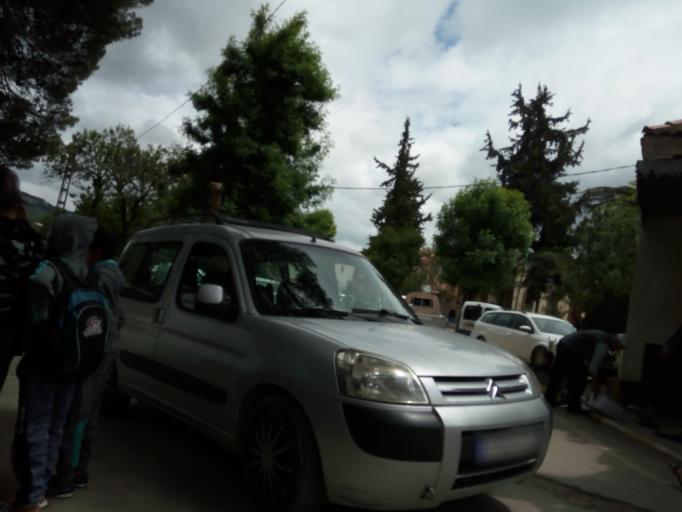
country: DZ
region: Setif
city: El Eulma
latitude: 36.3167
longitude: 5.7369
